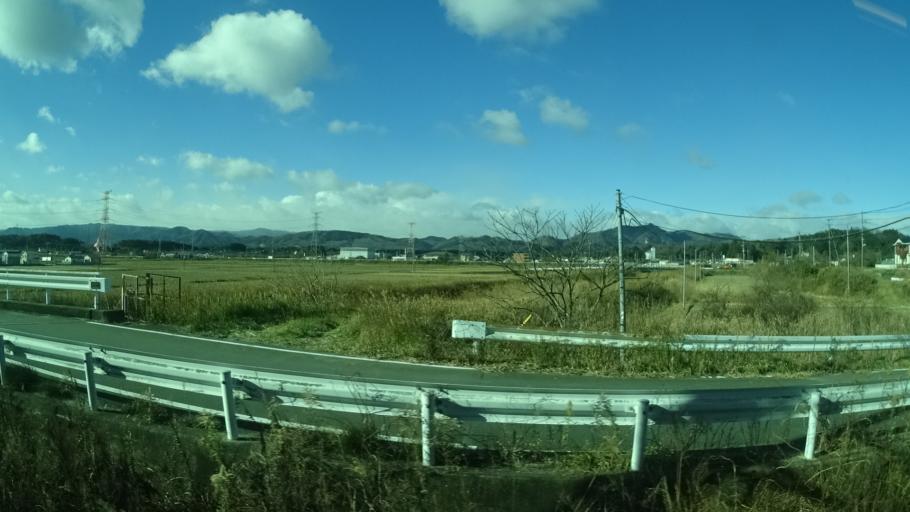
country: JP
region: Miyagi
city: Marumori
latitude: 37.8461
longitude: 140.9251
